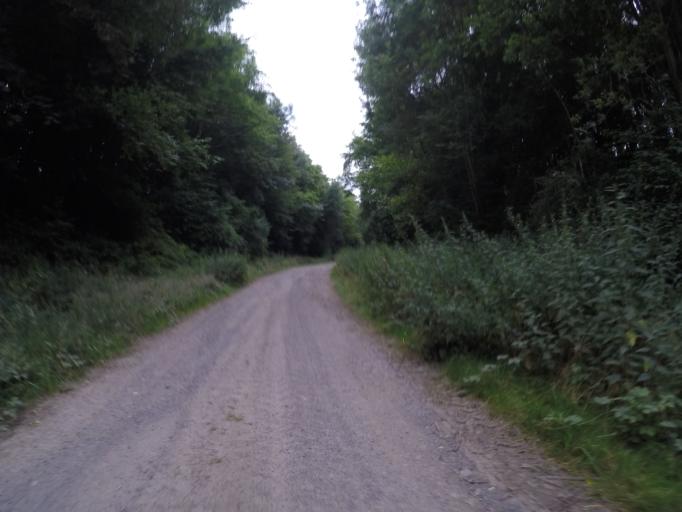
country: BE
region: Wallonia
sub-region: Province de Namur
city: Assesse
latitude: 50.2999
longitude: 5.0179
